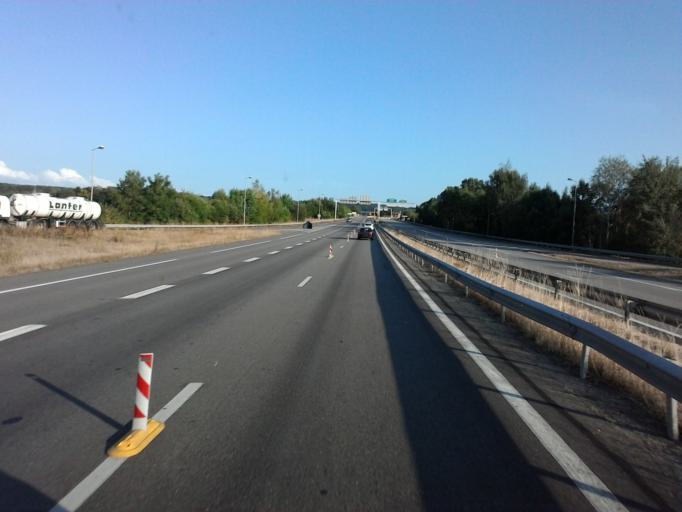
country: FR
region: Lorraine
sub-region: Departement des Vosges
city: Epinal
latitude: 48.1962
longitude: 6.4741
